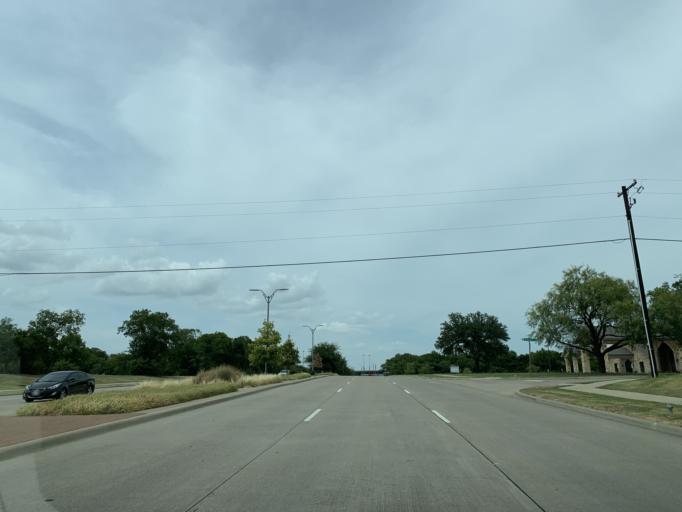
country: US
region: Texas
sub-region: Dallas County
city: Grand Prairie
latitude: 32.6699
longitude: -97.0235
